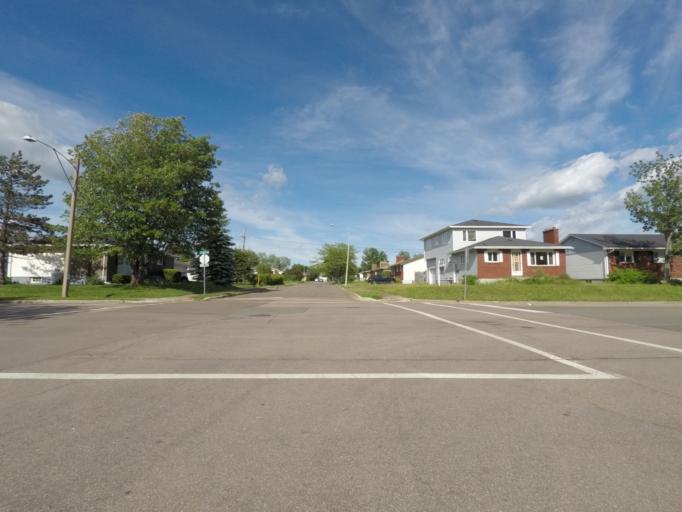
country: CA
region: New Brunswick
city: Moncton
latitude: 46.0991
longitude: -64.8281
